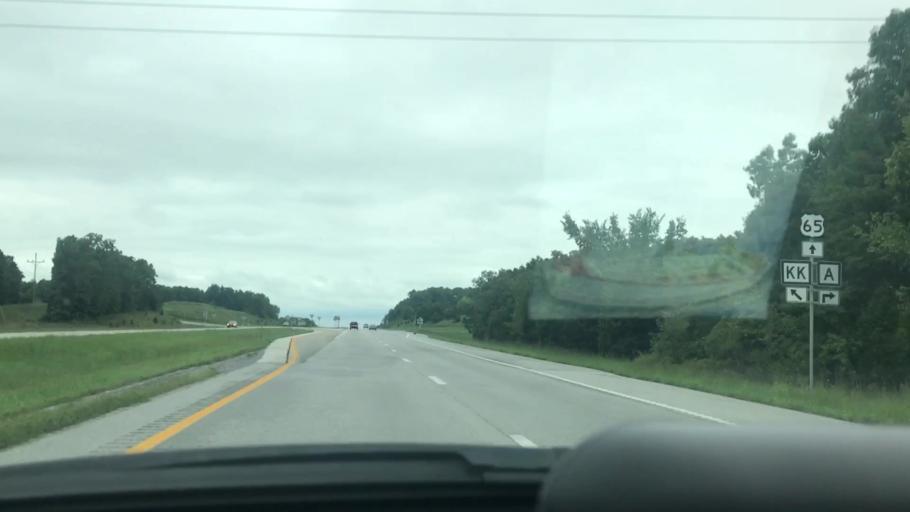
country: US
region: Missouri
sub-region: Greene County
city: Fair Grove
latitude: 37.3260
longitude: -93.1680
